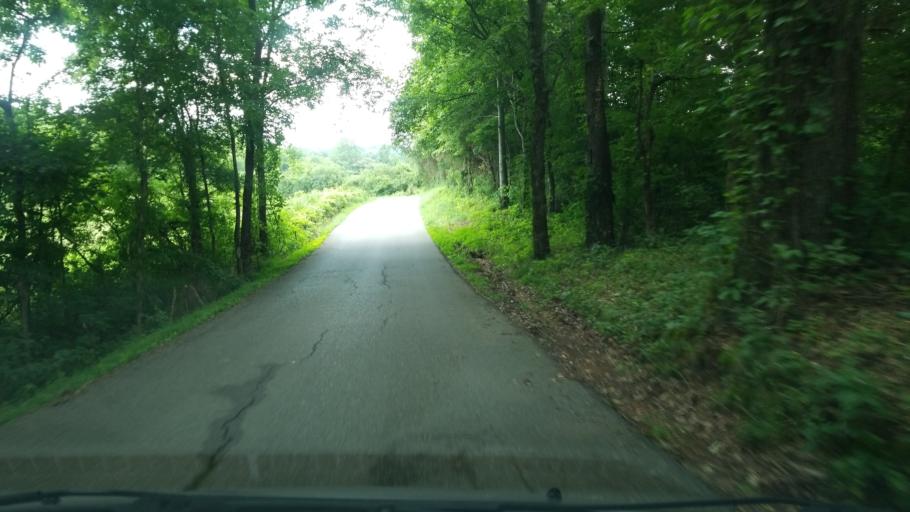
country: US
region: Tennessee
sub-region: Monroe County
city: Sweetwater
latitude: 35.6376
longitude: -84.5083
